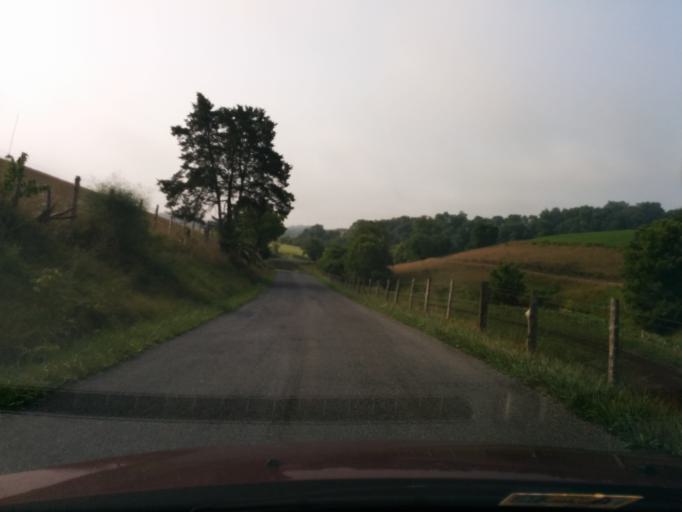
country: US
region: Virginia
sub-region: City of Lexington
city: Lexington
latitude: 37.7498
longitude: -79.5148
